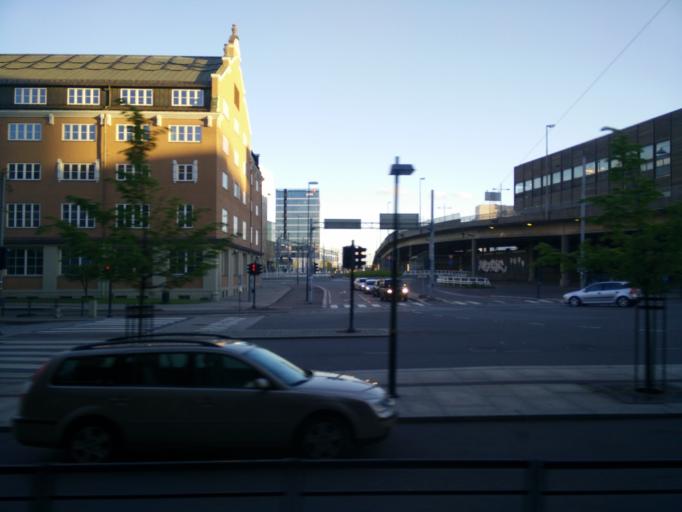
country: NO
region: Oslo
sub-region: Oslo
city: Oslo
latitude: 59.9113
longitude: 10.7583
